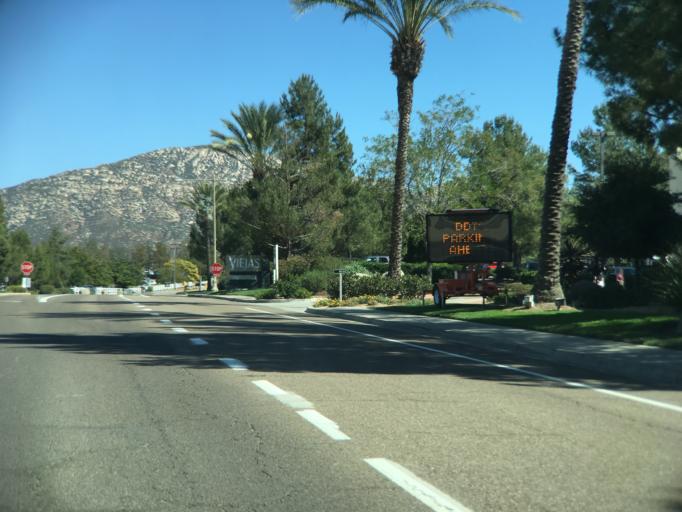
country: US
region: California
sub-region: San Diego County
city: Alpine
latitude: 32.8415
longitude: -116.7047
